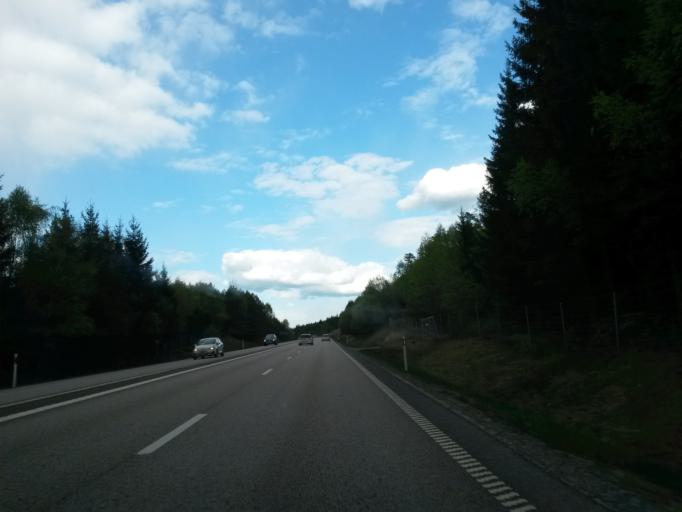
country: SE
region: Vaestra Goetaland
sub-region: Marks Kommun
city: Fritsla
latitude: 57.5144
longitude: 12.7536
